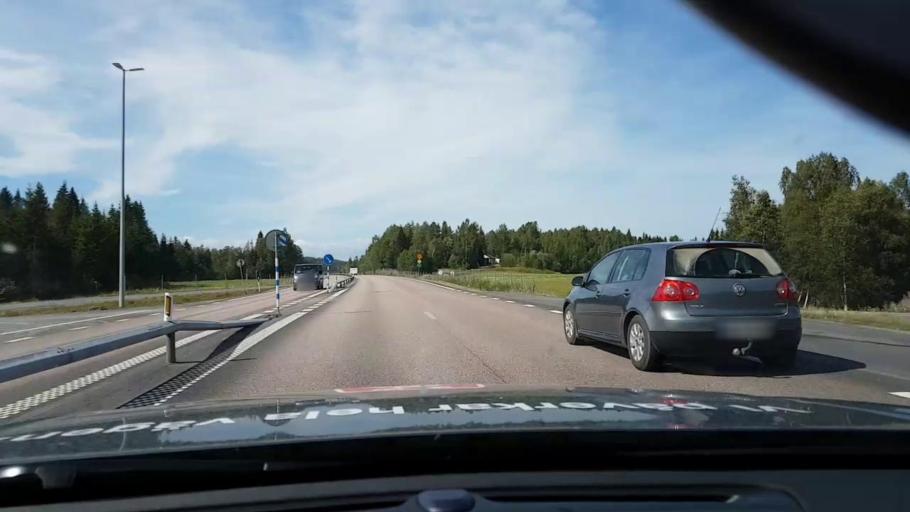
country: SE
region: Vaesternorrland
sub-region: OErnskoeldsviks Kommun
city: Ornskoldsvik
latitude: 63.3017
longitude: 18.8608
